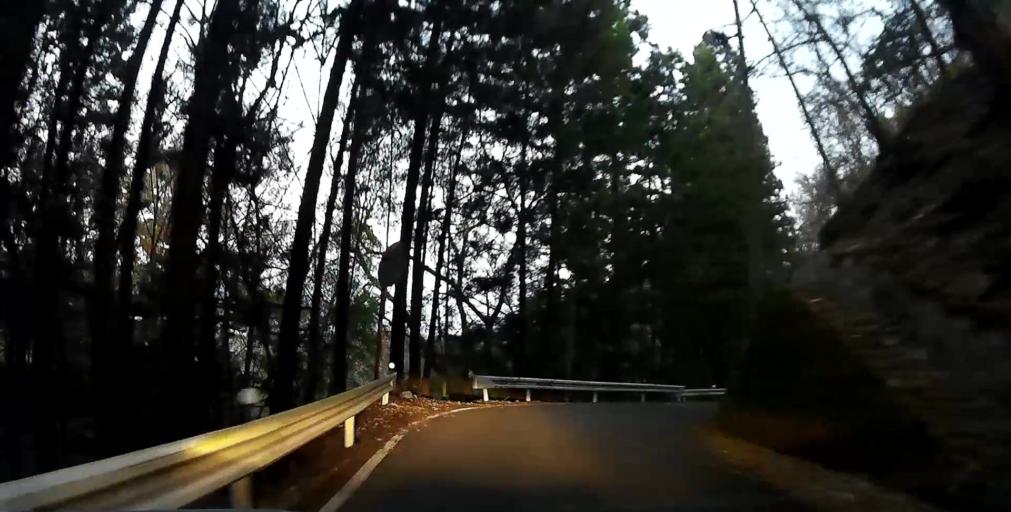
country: JP
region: Yamanashi
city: Uenohara
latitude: 35.6001
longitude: 139.1890
